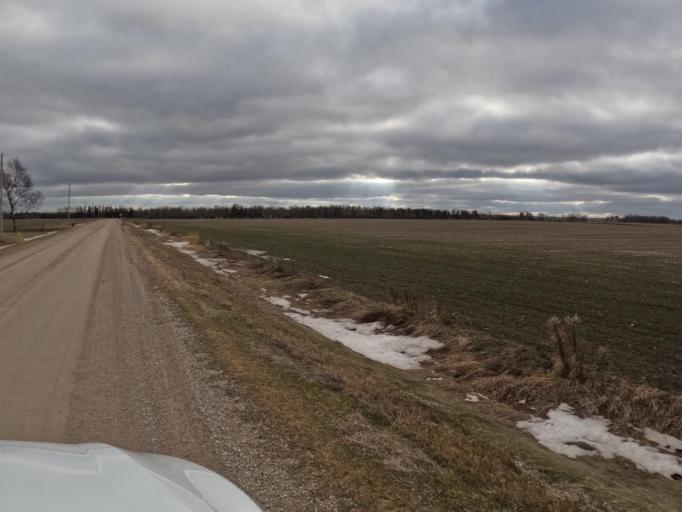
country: CA
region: Ontario
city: Shelburne
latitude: 43.8613
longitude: -80.3999
